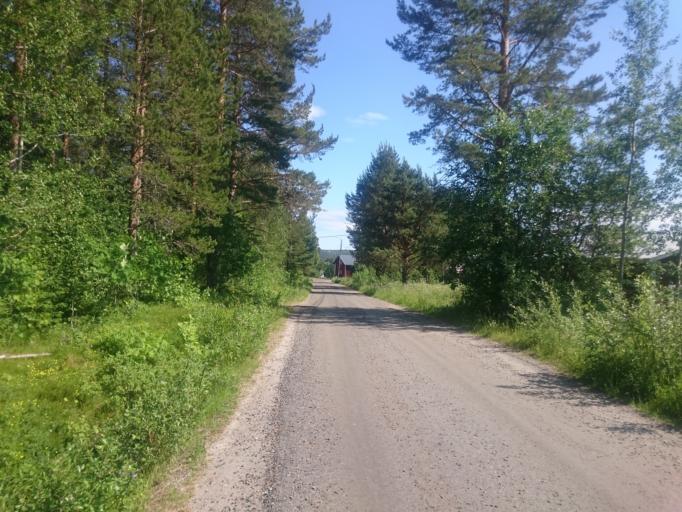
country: SE
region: Vaesternorrland
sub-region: OErnskoeldsviks Kommun
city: Bredbyn
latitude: 63.3007
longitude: 18.2633
